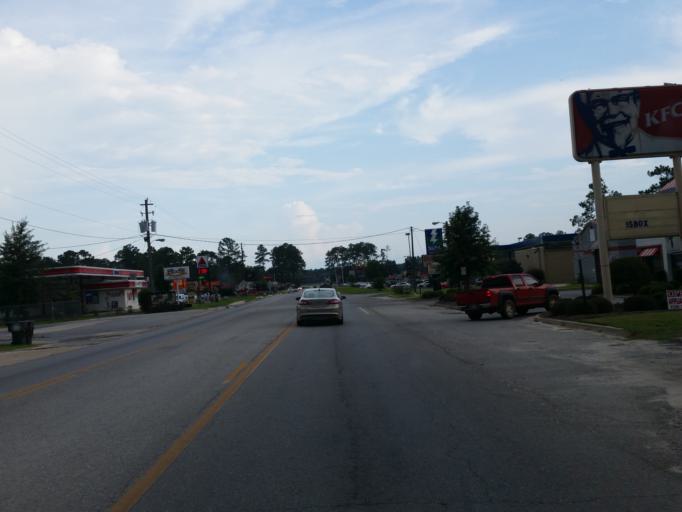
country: US
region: Georgia
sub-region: Berrien County
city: Nashville
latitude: 31.2020
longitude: -83.2509
